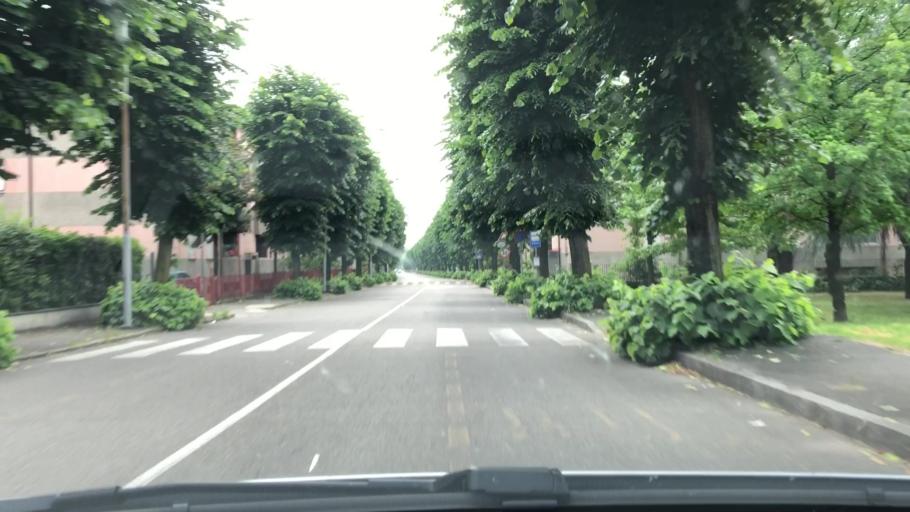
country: IT
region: Lombardy
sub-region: Provincia di Monza e Brianza
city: Desio
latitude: 45.6225
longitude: 9.1966
